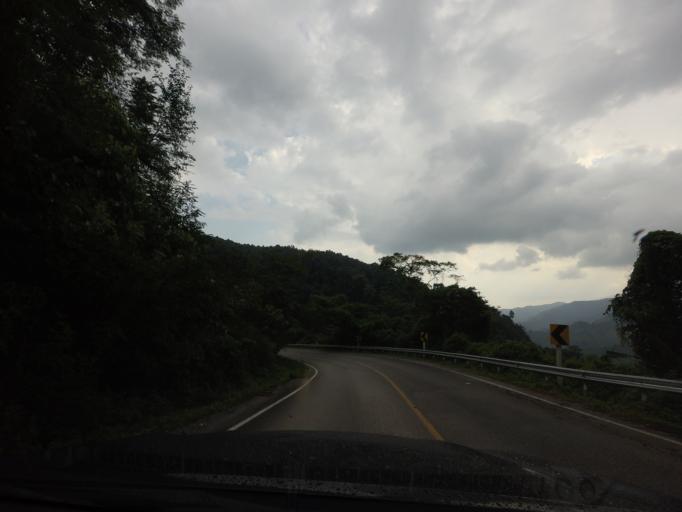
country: TH
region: Nan
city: Bo Kluea
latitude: 19.1665
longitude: 101.1435
